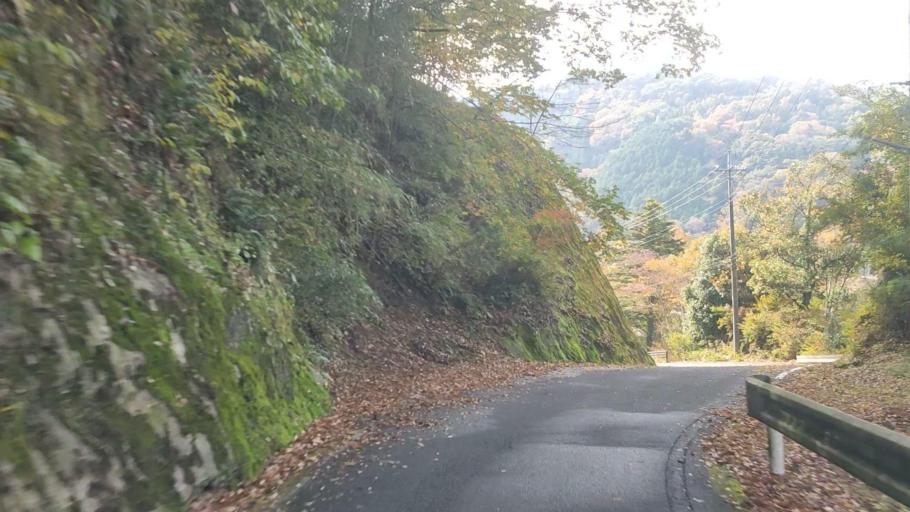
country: JP
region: Yamanashi
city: Ryuo
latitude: 35.4664
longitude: 138.4441
